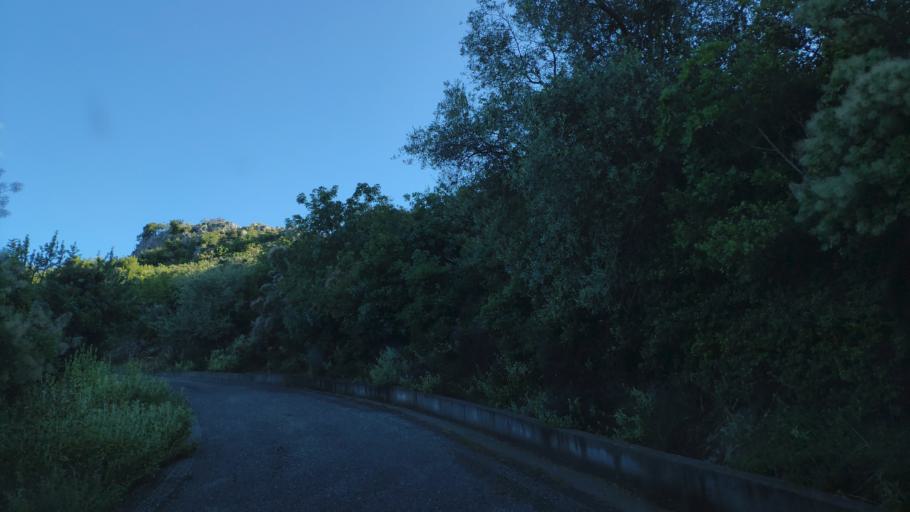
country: GR
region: West Greece
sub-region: Nomos Aitolias kai Akarnanias
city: Fitiai
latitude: 38.6608
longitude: 21.1926
